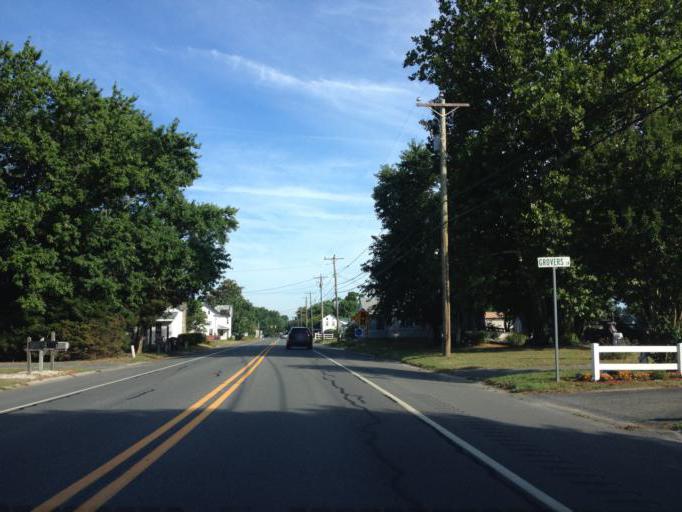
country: US
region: Delaware
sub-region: Sussex County
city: Selbyville
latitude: 38.4947
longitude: -75.1682
